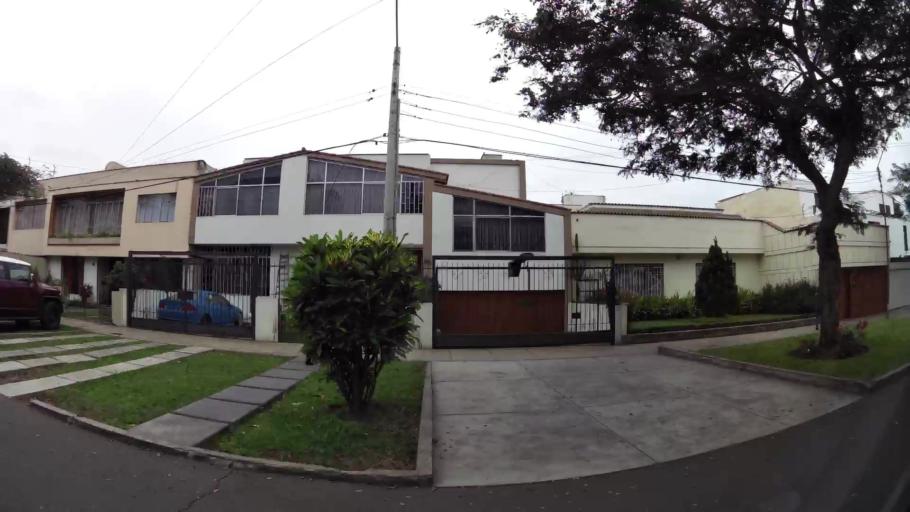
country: PE
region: Lima
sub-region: Lima
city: Surco
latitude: -12.1193
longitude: -77.0143
